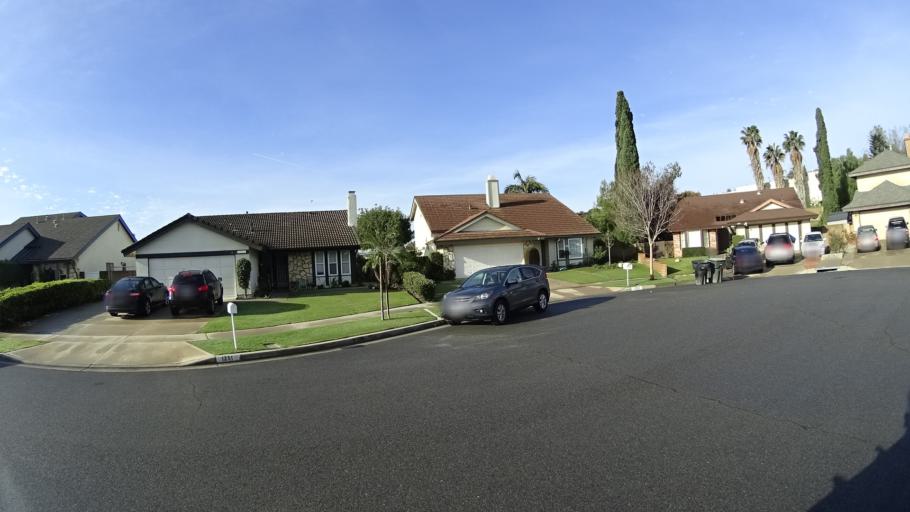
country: US
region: California
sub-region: Orange County
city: Yorba Linda
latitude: 33.8698
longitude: -117.7723
